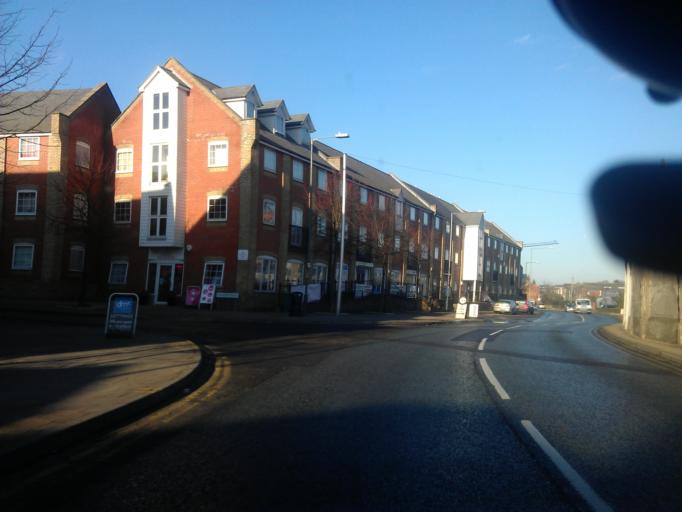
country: GB
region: England
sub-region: Essex
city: Colchester
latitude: 51.8816
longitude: 0.9263
